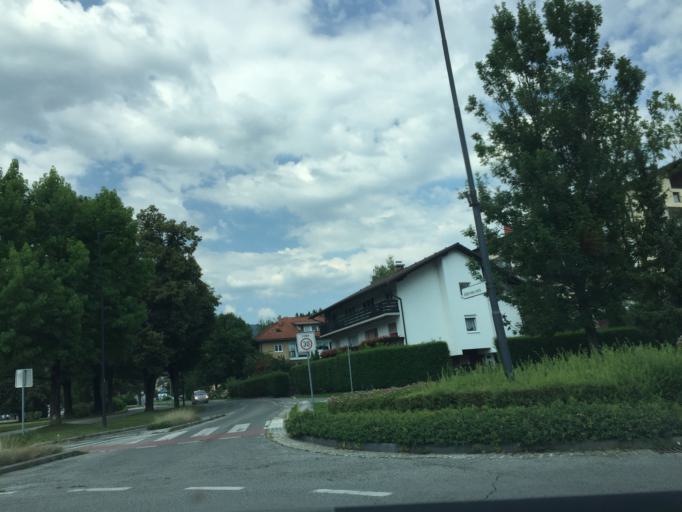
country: SI
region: Velenje
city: Velenje
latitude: 46.3650
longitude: 15.1074
